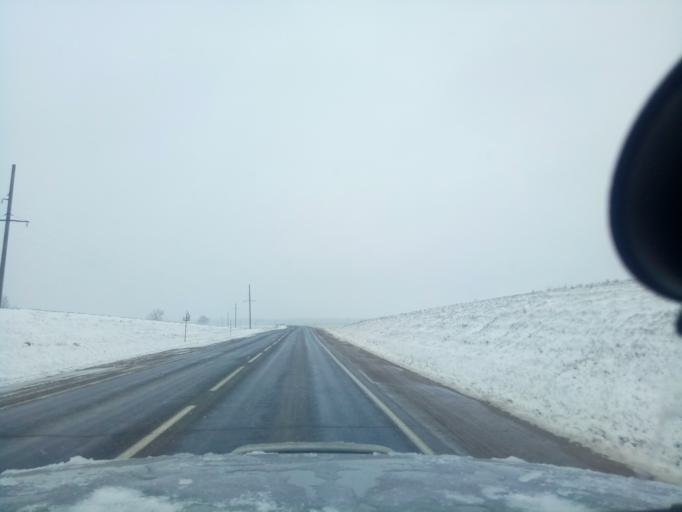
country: BY
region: Minsk
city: Nyasvizh
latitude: 53.2055
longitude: 26.6696
